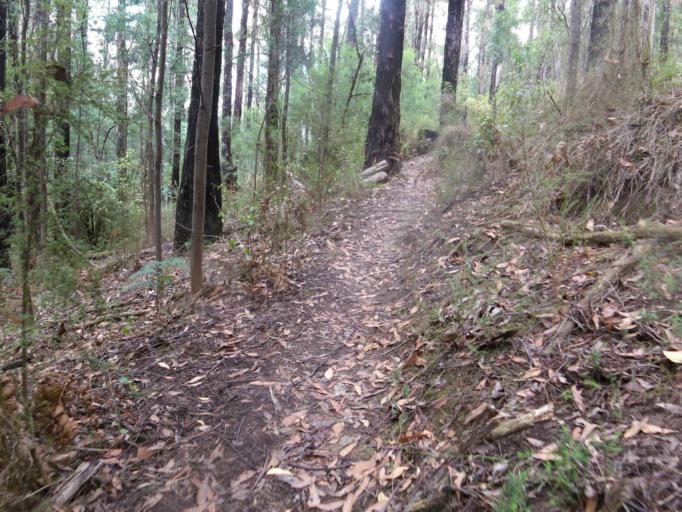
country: AU
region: Victoria
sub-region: Nillumbik
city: Saint Andrews
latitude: -37.5451
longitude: 145.3428
